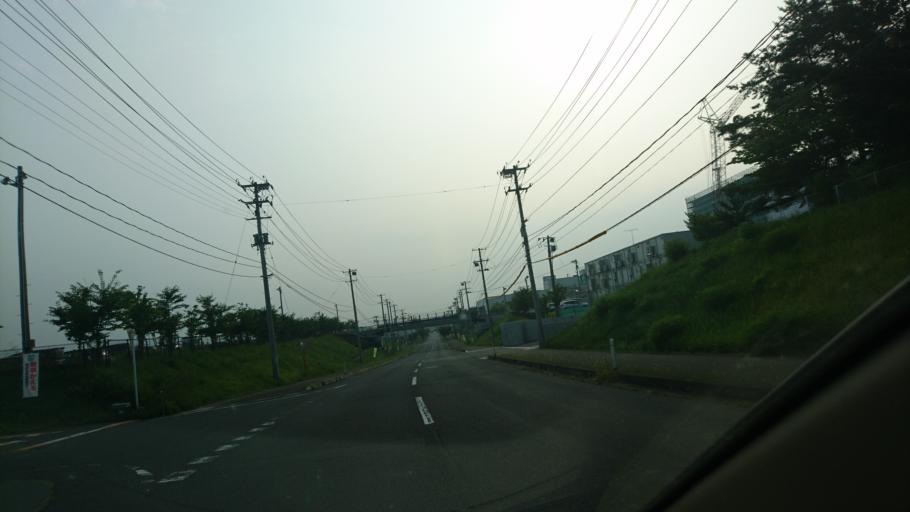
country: JP
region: Iwate
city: Mizusawa
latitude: 39.2141
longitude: 141.1887
